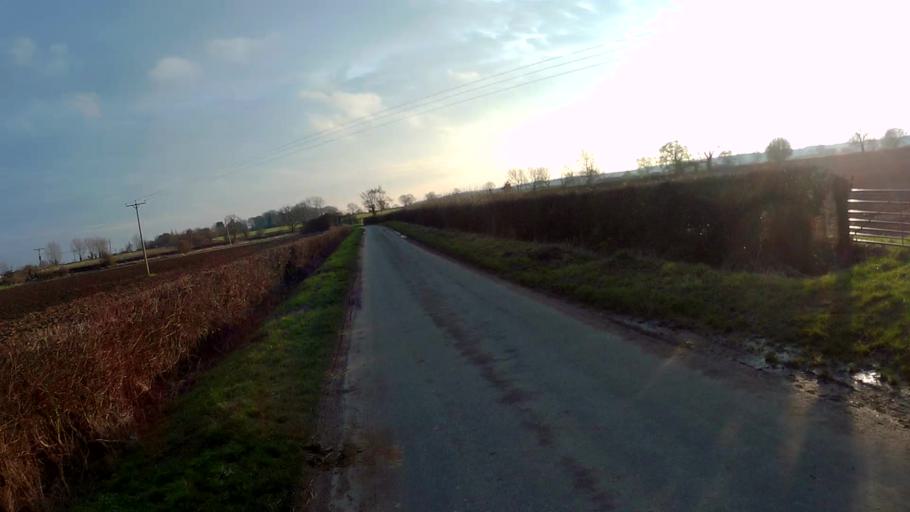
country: GB
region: England
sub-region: Lincolnshire
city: Bourne
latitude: 52.8097
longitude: -0.3978
